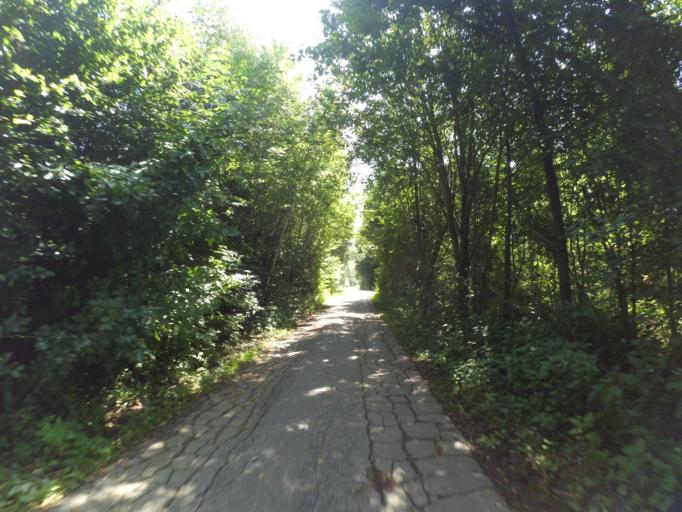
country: DE
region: Bavaria
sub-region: Swabia
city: Baisweil
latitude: 47.9828
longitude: 10.5676
